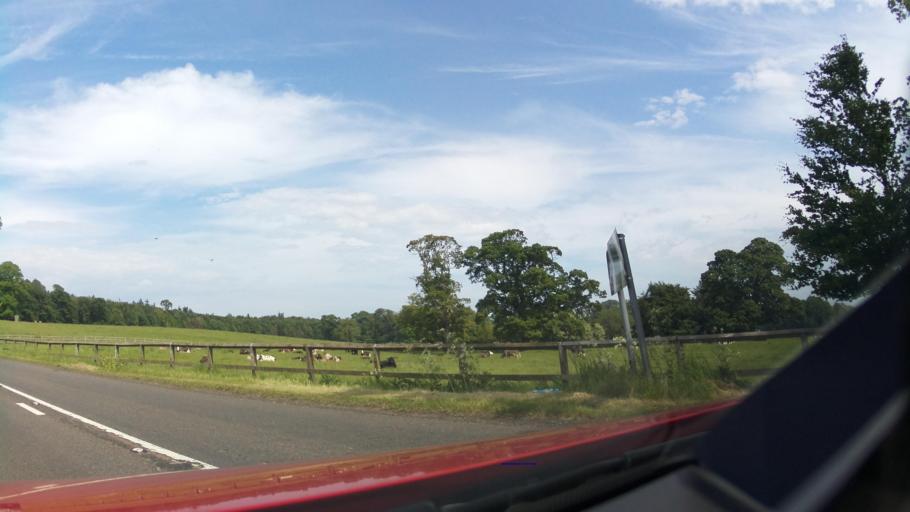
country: GB
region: England
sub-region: Northumberland
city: Alnwick
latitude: 55.4229
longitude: -1.7043
